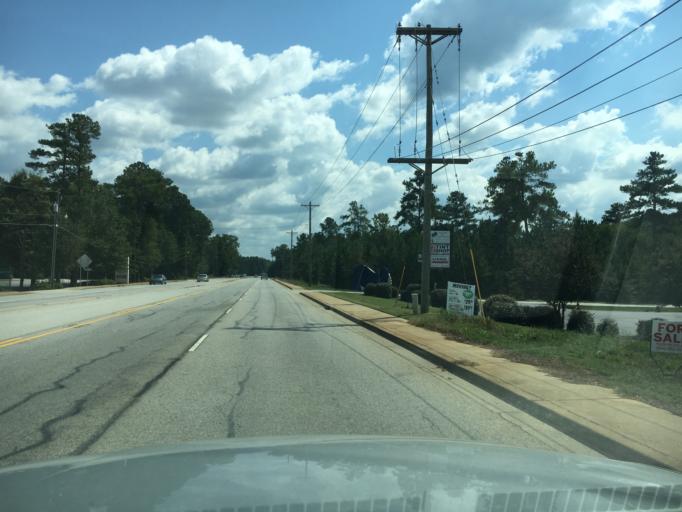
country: US
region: South Carolina
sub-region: Greenwood County
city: Greenwood
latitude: 34.2017
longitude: -82.1980
